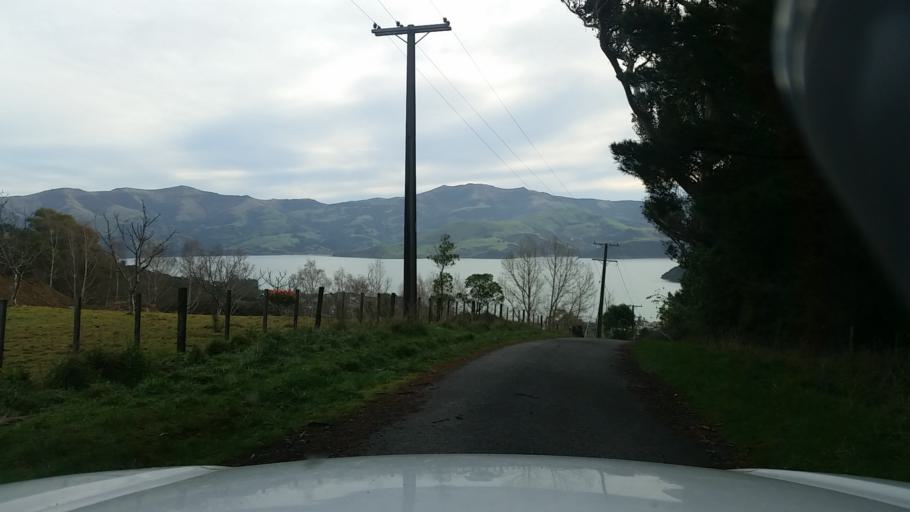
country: NZ
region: Canterbury
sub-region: Christchurch City
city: Christchurch
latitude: -43.8090
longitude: 172.9829
